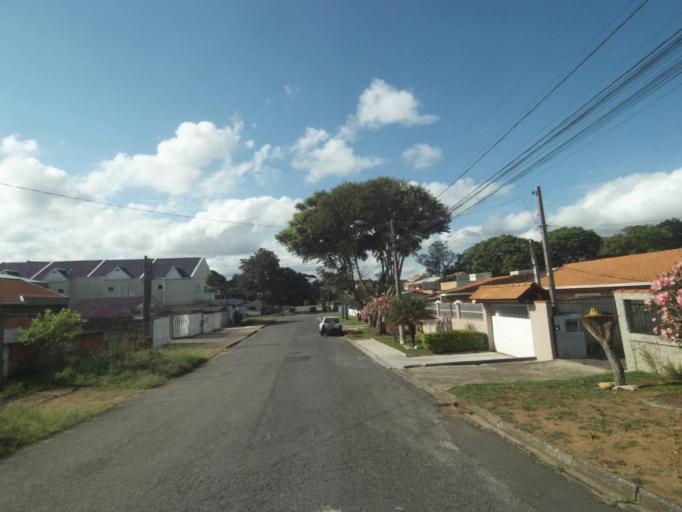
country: BR
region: Parana
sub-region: Curitiba
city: Curitiba
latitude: -25.3896
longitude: -49.3019
